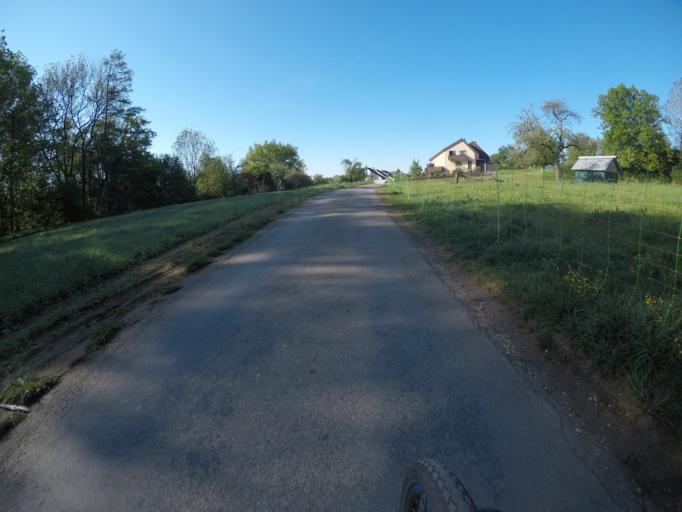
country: DE
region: Baden-Wuerttemberg
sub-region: Regierungsbezirk Stuttgart
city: Neckartailfingen
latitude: 48.6315
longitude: 9.2647
